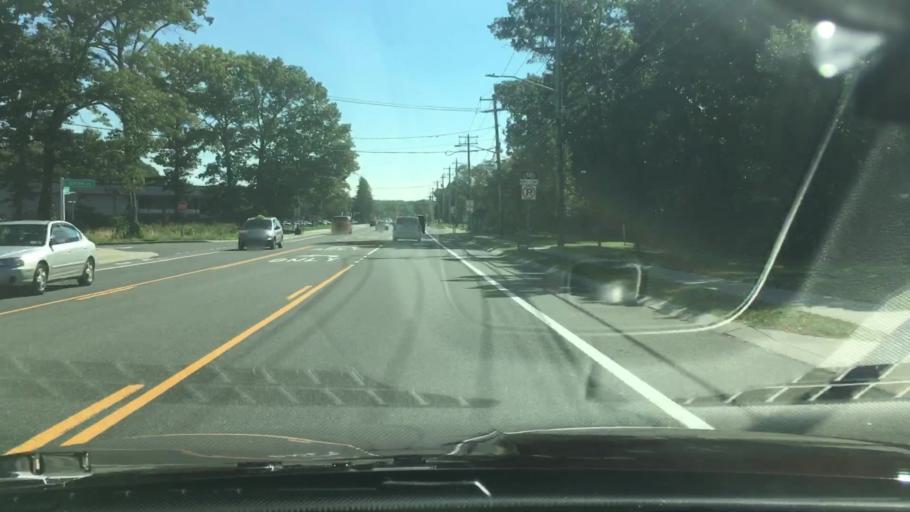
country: US
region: New York
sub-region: Suffolk County
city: Port Jefferson Station
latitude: 40.9168
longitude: -73.0359
